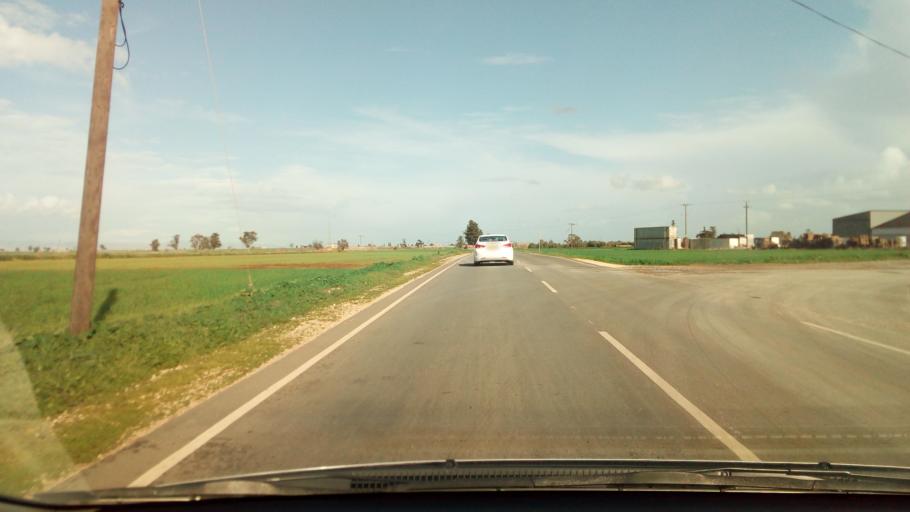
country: CY
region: Ammochostos
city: Achna
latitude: 35.0422
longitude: 33.7678
